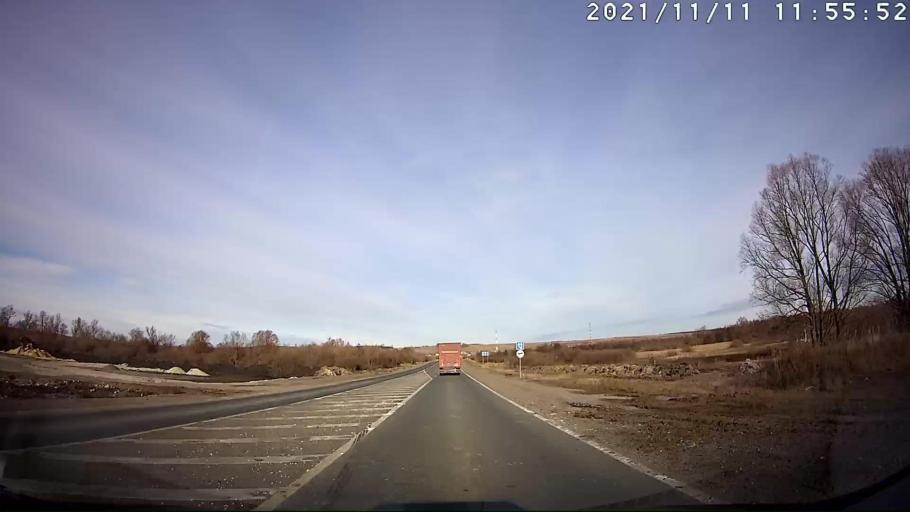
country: RU
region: Samara
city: Balasheyka
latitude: 53.5444
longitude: 48.3348
